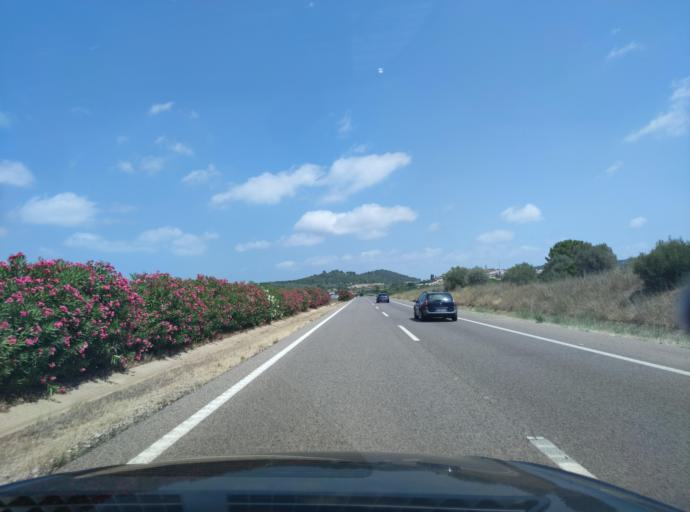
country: ES
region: Catalonia
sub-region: Provincia de Tarragona
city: Santa Barbara
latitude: 40.6618
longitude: 0.5117
